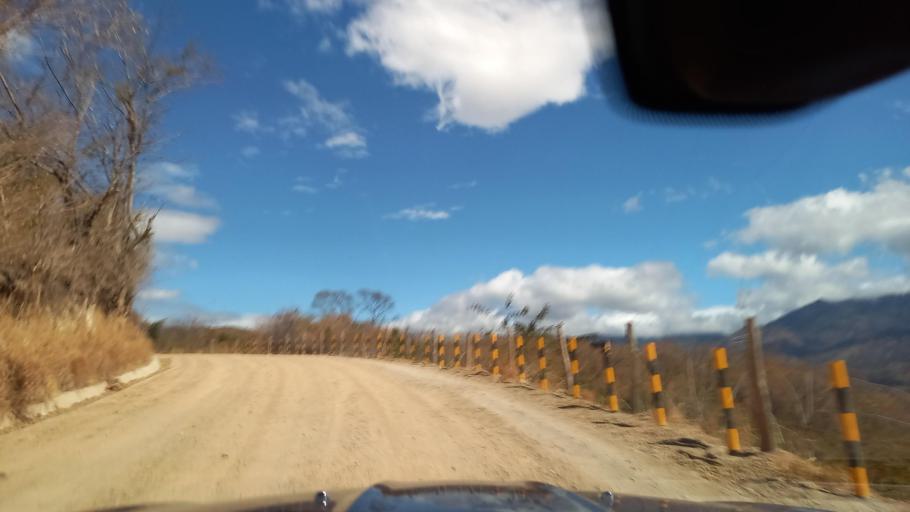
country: SV
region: Santa Ana
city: Metapan
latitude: 14.3600
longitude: -89.4808
